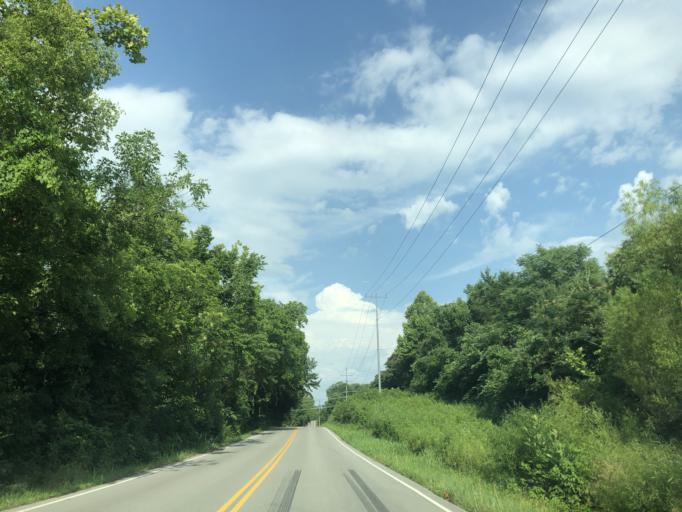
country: US
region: Tennessee
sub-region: Davidson County
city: Lakewood
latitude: 36.1220
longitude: -86.6548
